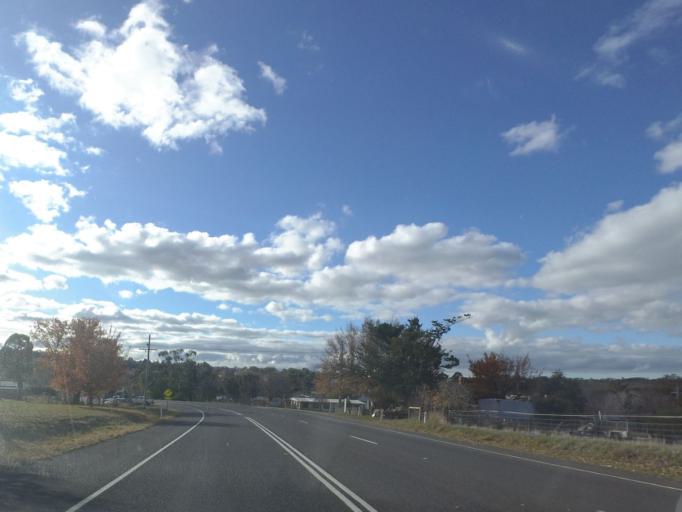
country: AU
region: Victoria
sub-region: Mount Alexander
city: Castlemaine
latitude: -37.1427
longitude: 144.3504
